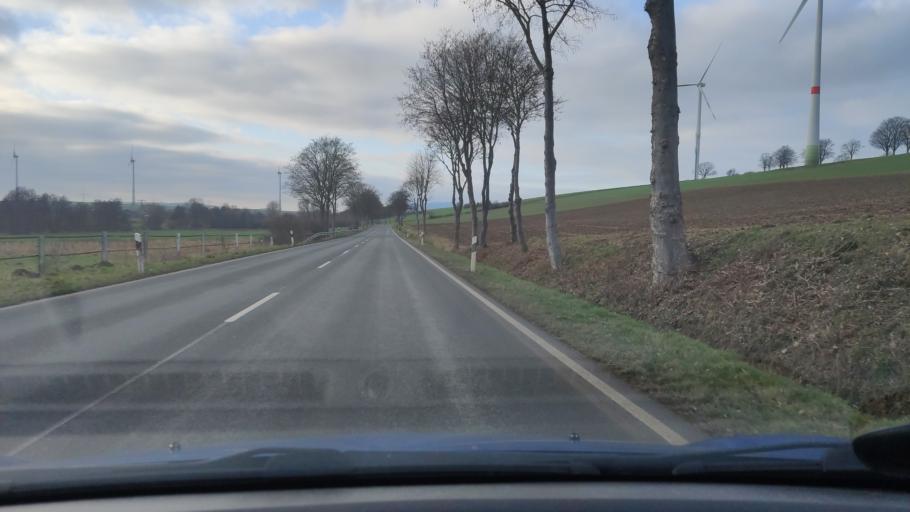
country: DE
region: Lower Saxony
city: Coppenbrugge
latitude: 52.1352
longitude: 9.5362
